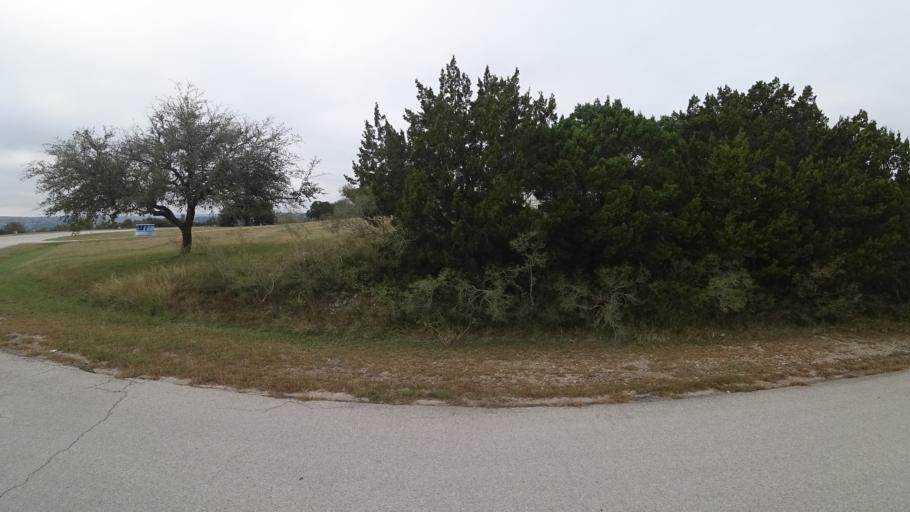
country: US
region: Texas
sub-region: Travis County
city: Hudson Bend
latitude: 30.3951
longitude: -97.9091
